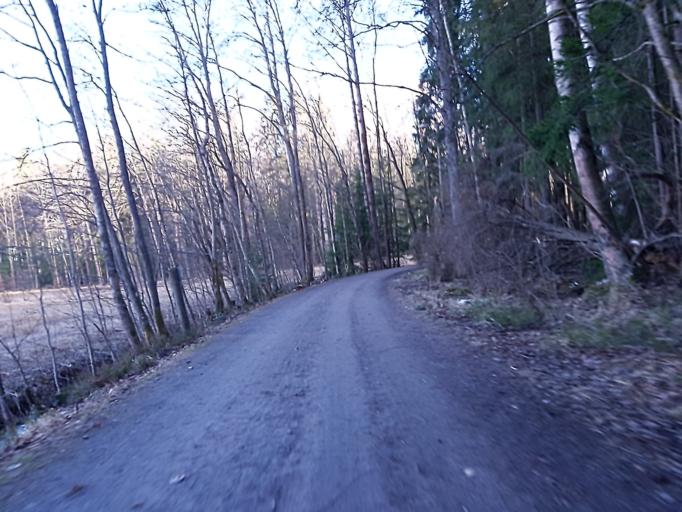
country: FI
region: Uusimaa
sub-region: Helsinki
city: Helsinki
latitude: 60.2688
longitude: 24.9347
